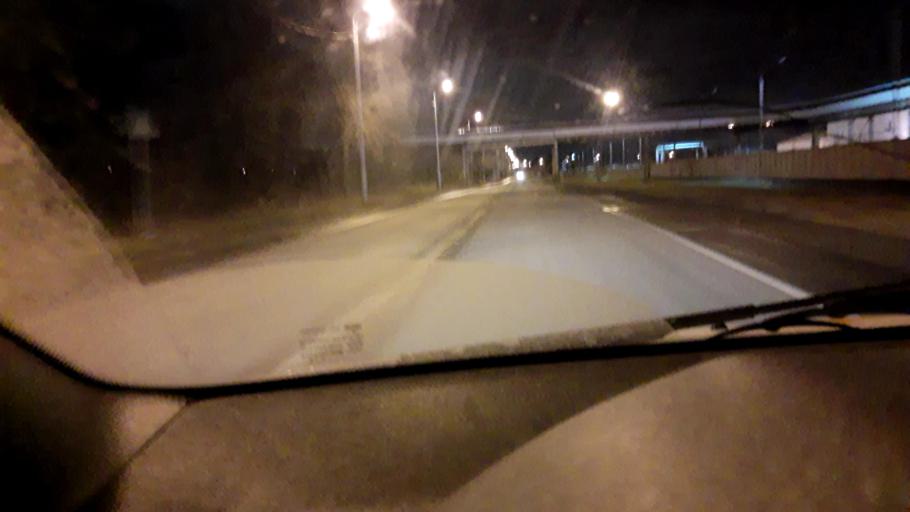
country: RU
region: Bashkortostan
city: Blagoveshchensk
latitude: 54.9154
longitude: 56.0653
